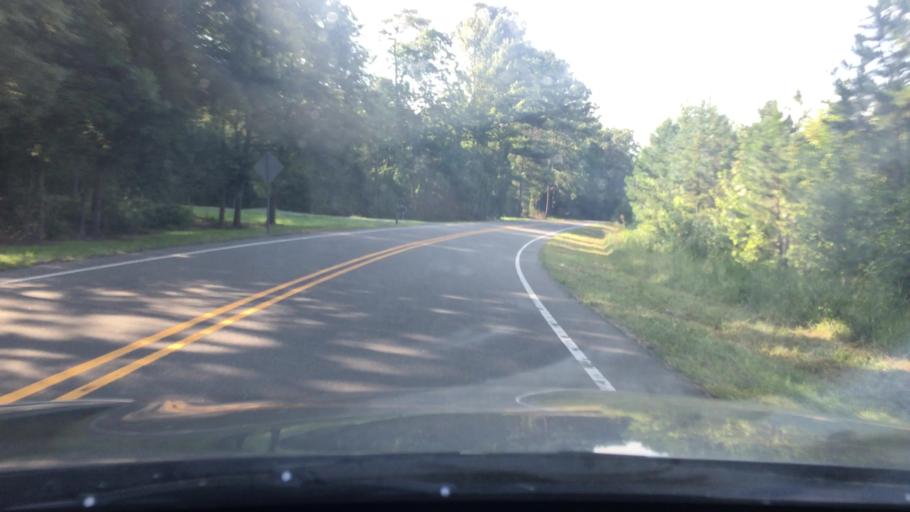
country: US
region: North Carolina
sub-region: Alamance County
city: Green Level
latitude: 36.2535
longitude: -79.3321
